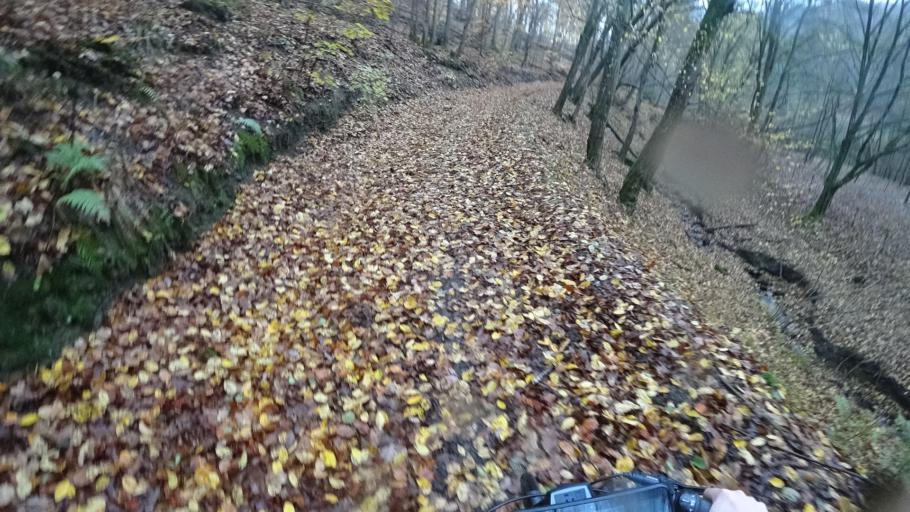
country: DE
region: Rheinland-Pfalz
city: Bad Neuenahr-Ahrweiler
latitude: 50.5041
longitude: 7.0902
